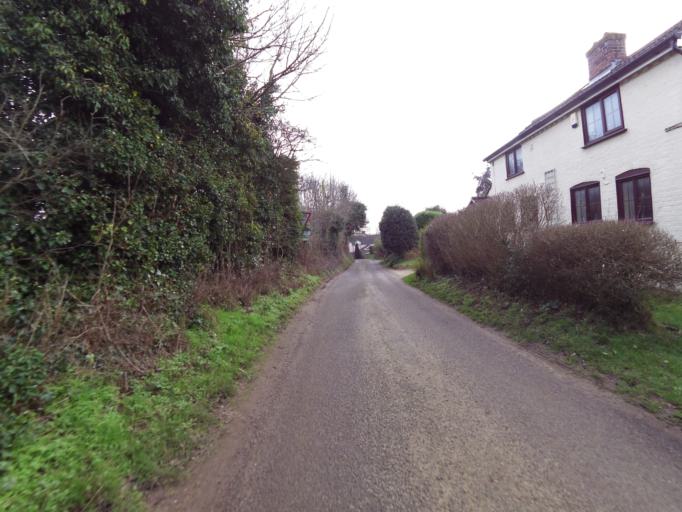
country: GB
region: England
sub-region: Suffolk
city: Woodbridge
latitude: 52.0570
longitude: 1.3187
